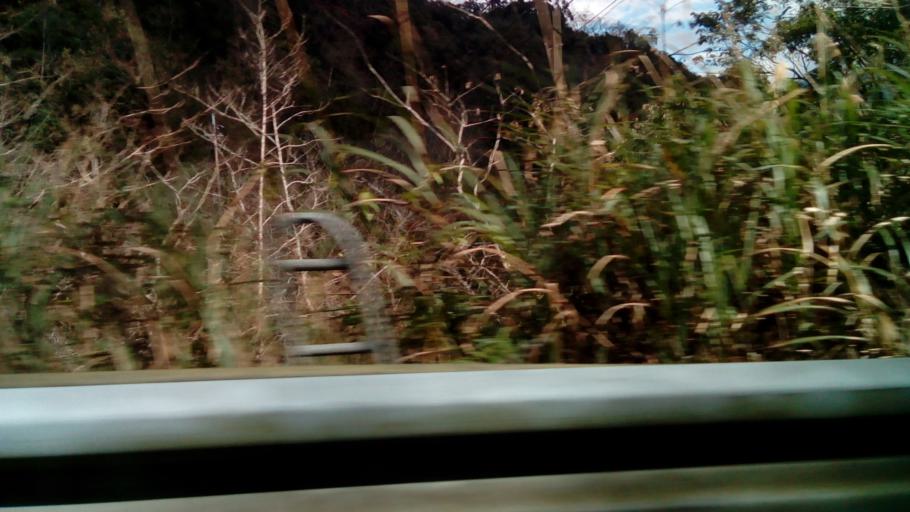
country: TW
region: Taiwan
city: Daxi
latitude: 24.4122
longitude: 121.3601
